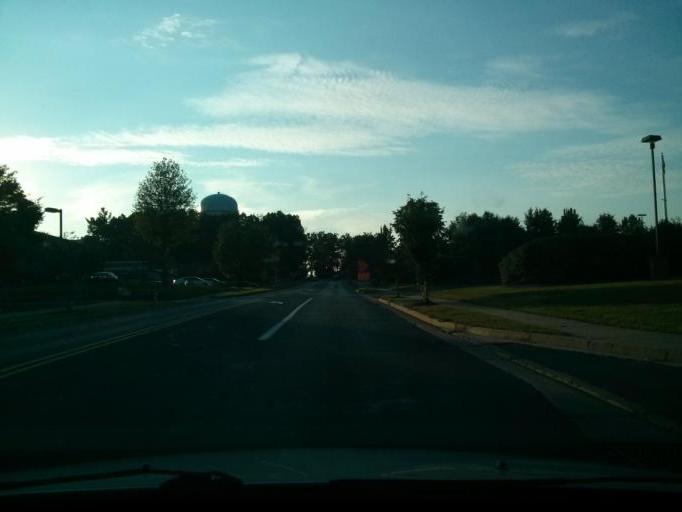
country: US
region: Pennsylvania
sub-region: Centre County
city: Park Forest Village
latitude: 40.8041
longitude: -77.8906
